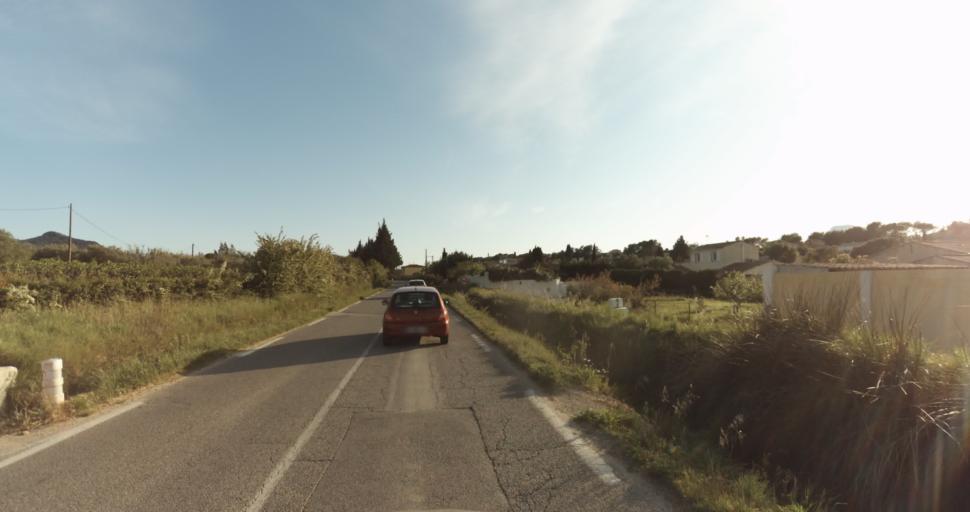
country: FR
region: Provence-Alpes-Cote d'Azur
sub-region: Departement du Var
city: La Crau
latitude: 43.1624
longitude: 6.1003
